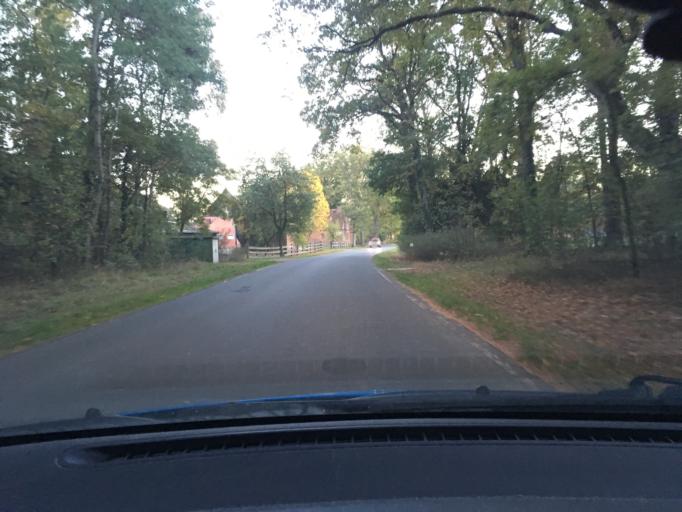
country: DE
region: Lower Saxony
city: Neetze
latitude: 53.2884
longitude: 10.6170
